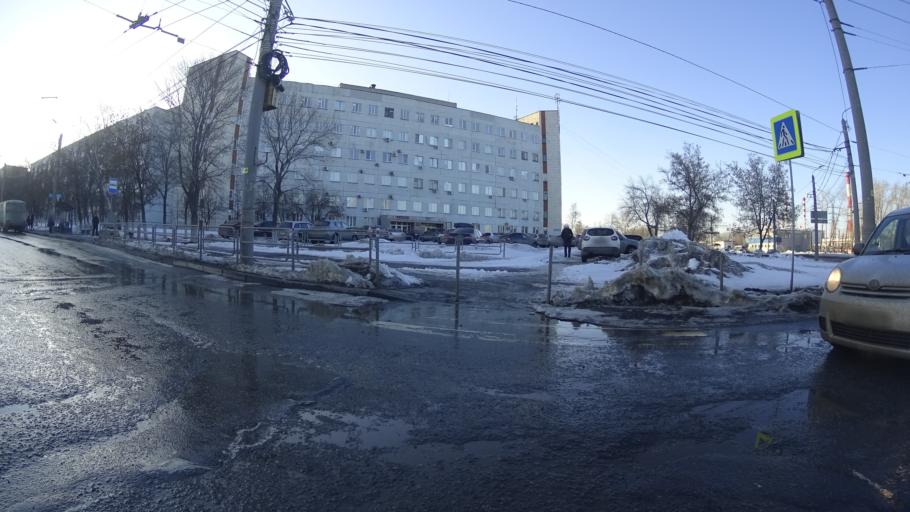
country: RU
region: Chelyabinsk
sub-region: Gorod Chelyabinsk
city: Chelyabinsk
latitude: 55.1278
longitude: 61.4795
